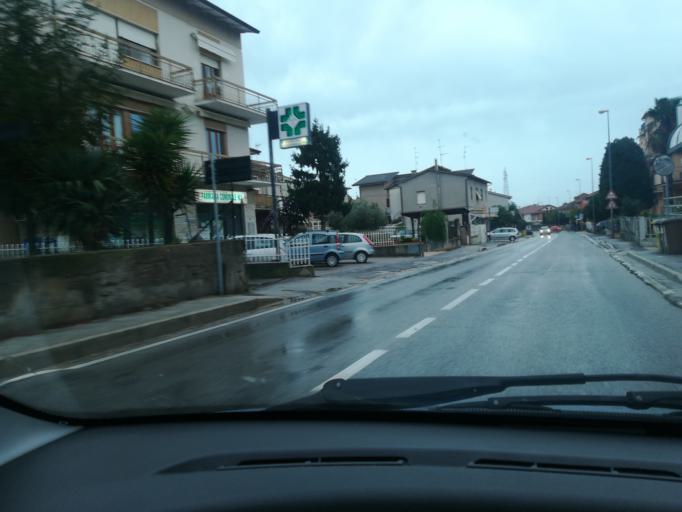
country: IT
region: The Marches
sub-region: Provincia di Macerata
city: Santa Maria Apparente
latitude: 43.2971
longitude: 13.6921
